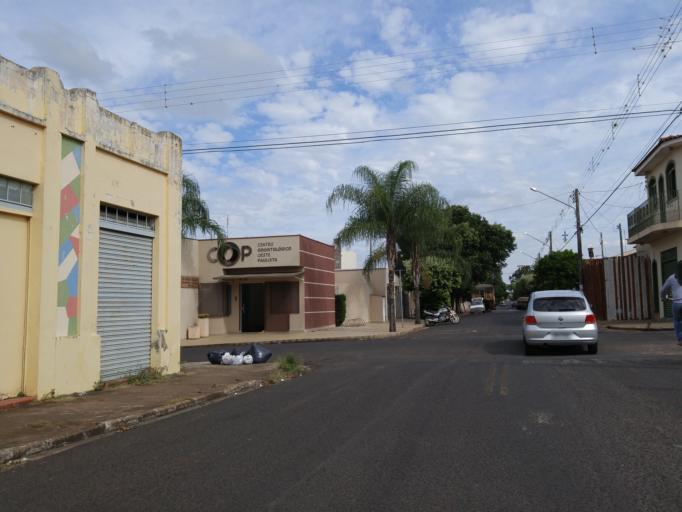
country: BR
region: Sao Paulo
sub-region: Paraguacu Paulista
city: Paraguacu Paulista
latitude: -22.4169
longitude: -50.5769
